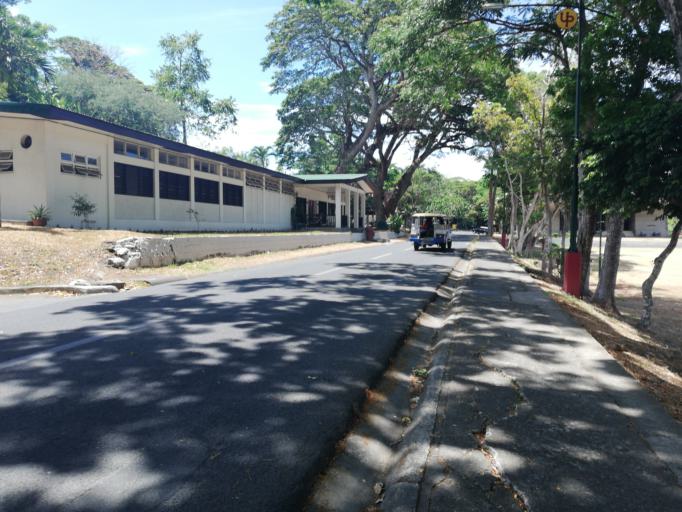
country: PH
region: Calabarzon
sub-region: Province of Laguna
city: Los Banos
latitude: 14.1625
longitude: 121.2406
